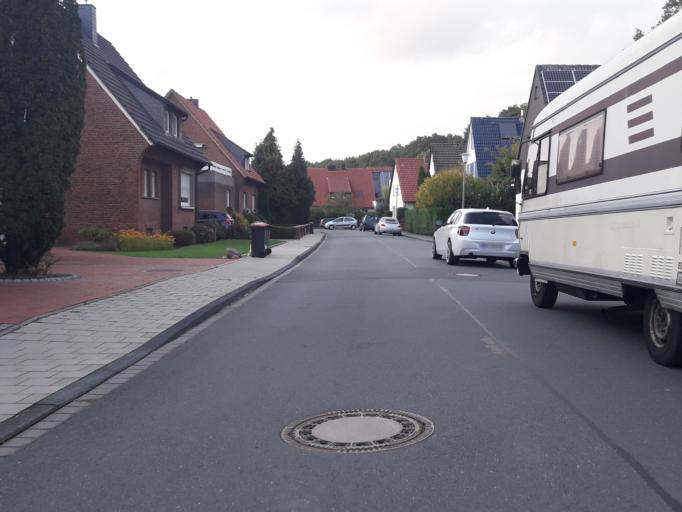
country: DE
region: North Rhine-Westphalia
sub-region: Regierungsbezirk Munster
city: Muenster
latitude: 51.9076
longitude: 7.6637
